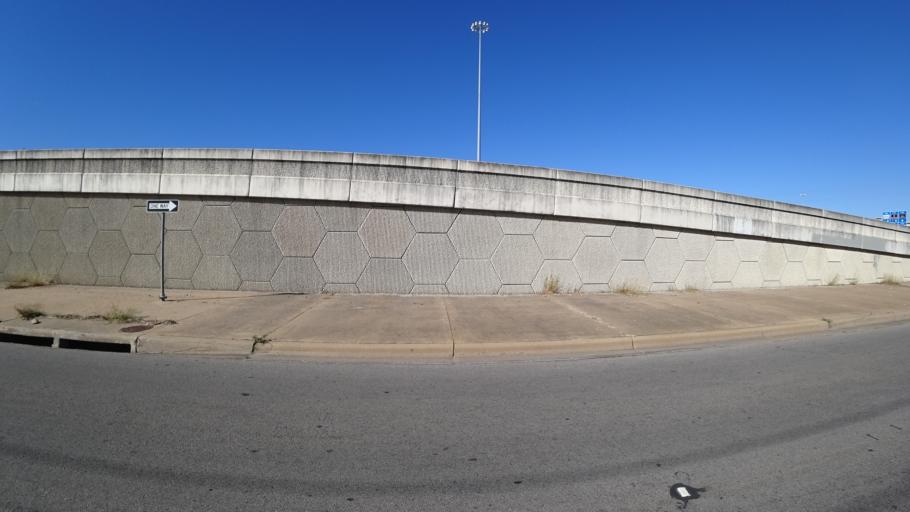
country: US
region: Texas
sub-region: Travis County
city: Rollingwood
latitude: 30.2322
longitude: -97.7993
